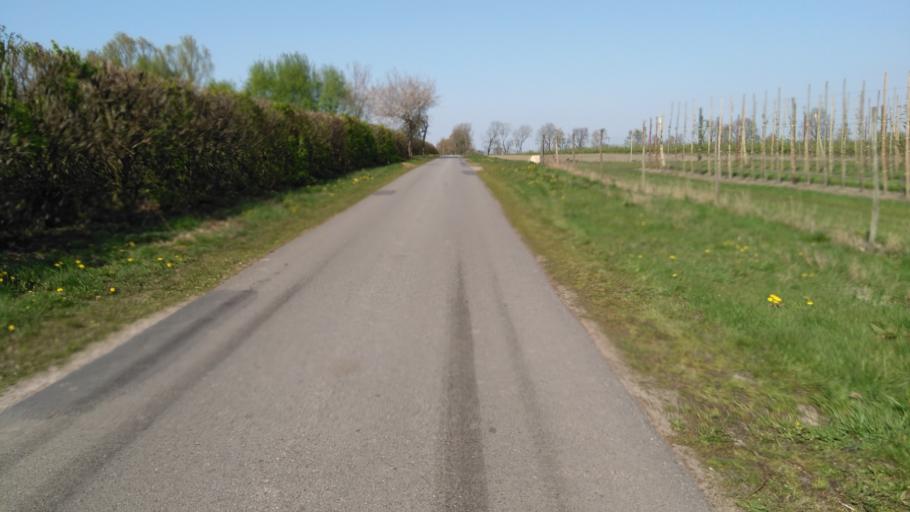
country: DE
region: Lower Saxony
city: Bliedersdorf
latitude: 53.4673
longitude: 9.5670
